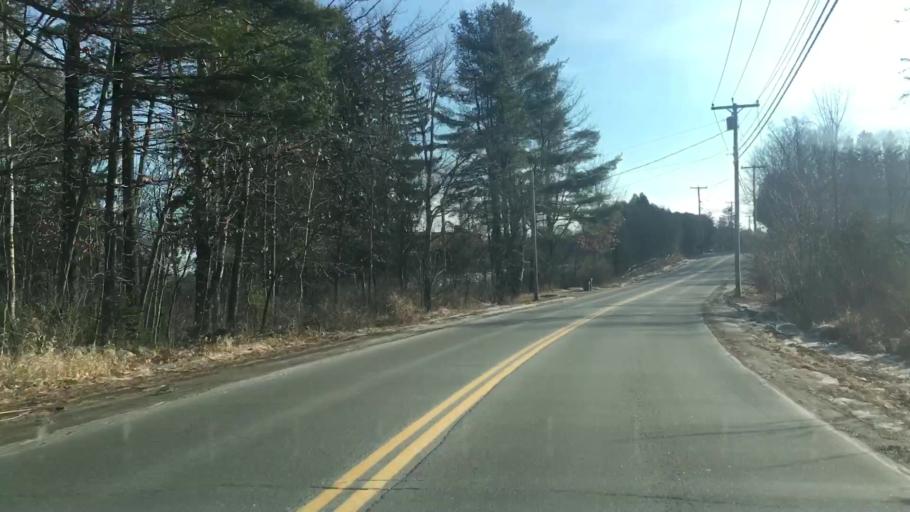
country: US
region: Maine
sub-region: Androscoggin County
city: Auburn
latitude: 44.1255
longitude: -70.2631
